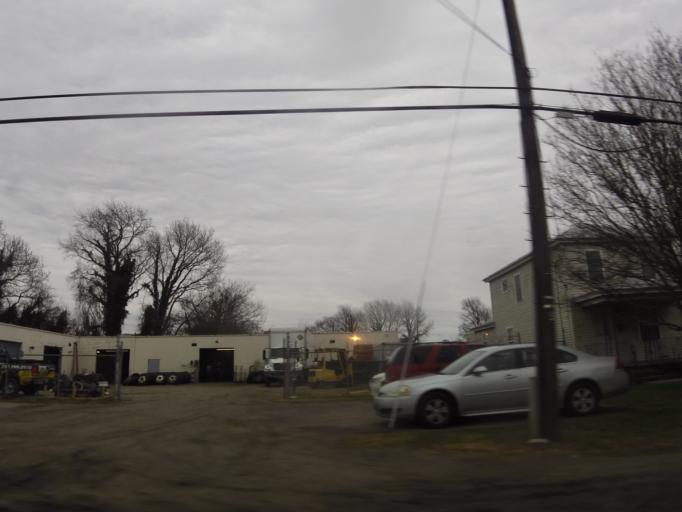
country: US
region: Virginia
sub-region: City of Portsmouth
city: Portsmouth
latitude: 36.8440
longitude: -76.3325
